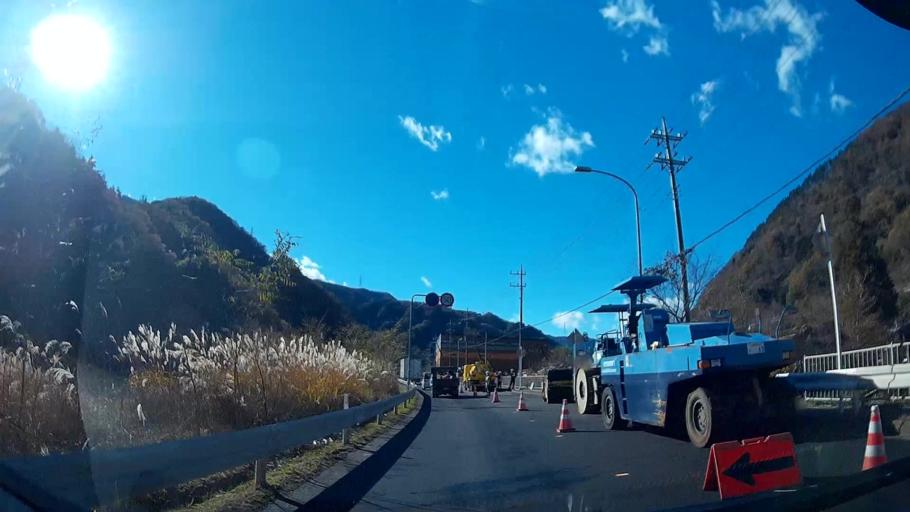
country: JP
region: Yamanashi
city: Otsuki
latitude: 35.6031
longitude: 138.8569
